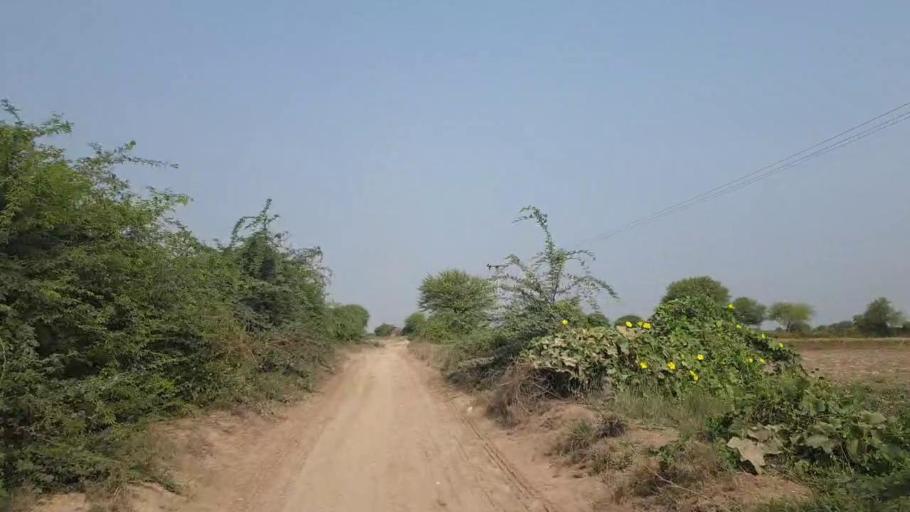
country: PK
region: Sindh
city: Badin
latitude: 24.6989
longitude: 68.7776
